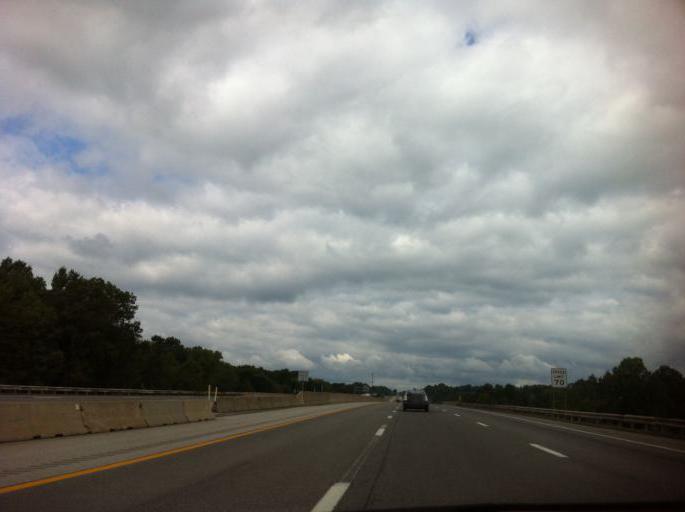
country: US
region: Ohio
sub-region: Trumbull County
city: Newton Falls
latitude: 41.2226
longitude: -80.9601
